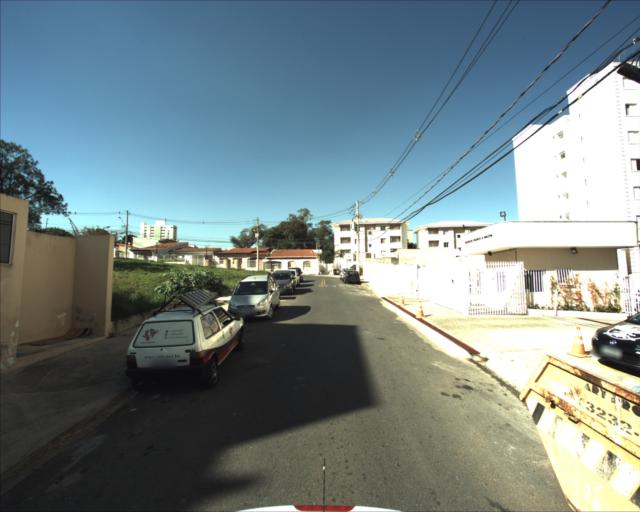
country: BR
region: Sao Paulo
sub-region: Sorocaba
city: Sorocaba
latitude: -23.4929
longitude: -47.4287
